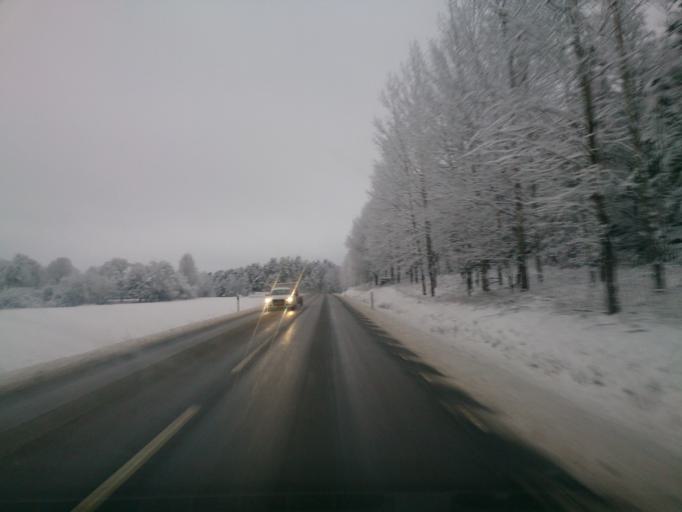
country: SE
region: OEstergoetland
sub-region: Atvidabergs Kommun
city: Atvidaberg
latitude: 58.2823
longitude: 15.9024
